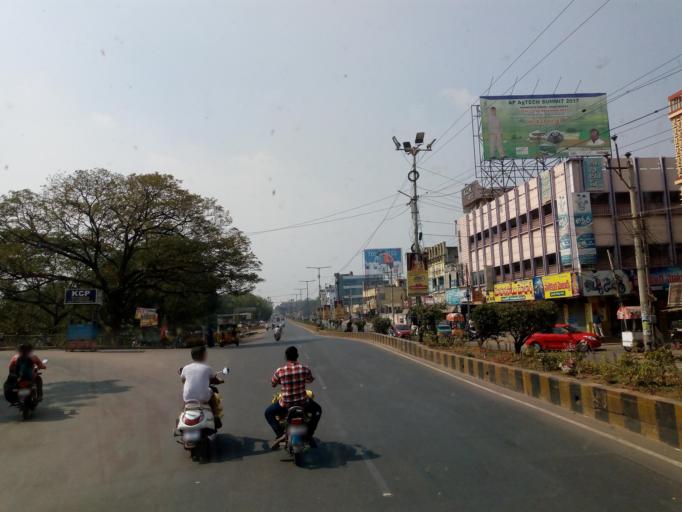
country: IN
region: Andhra Pradesh
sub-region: West Godavari
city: Eluru
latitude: 16.7094
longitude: 81.1048
